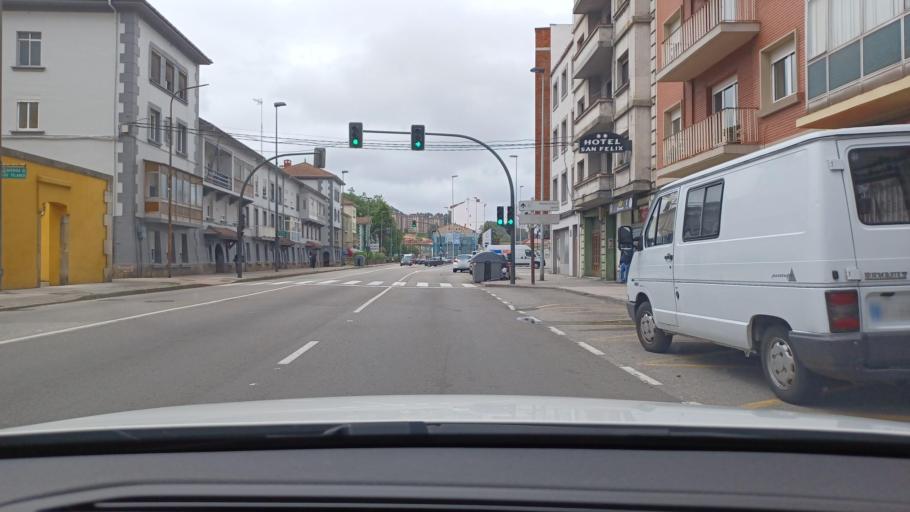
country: ES
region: Asturias
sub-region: Province of Asturias
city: Aviles
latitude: 43.5638
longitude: -5.9254
